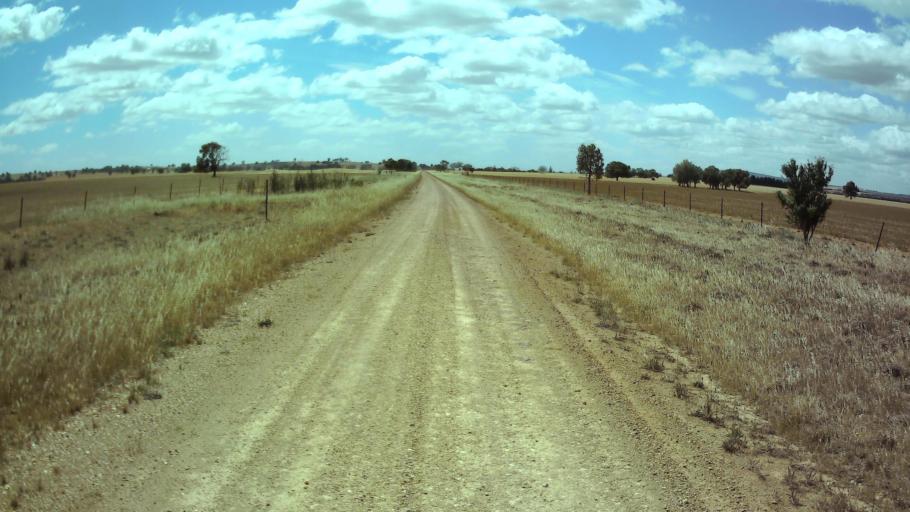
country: AU
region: New South Wales
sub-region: Weddin
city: Grenfell
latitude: -33.9884
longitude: 148.3160
